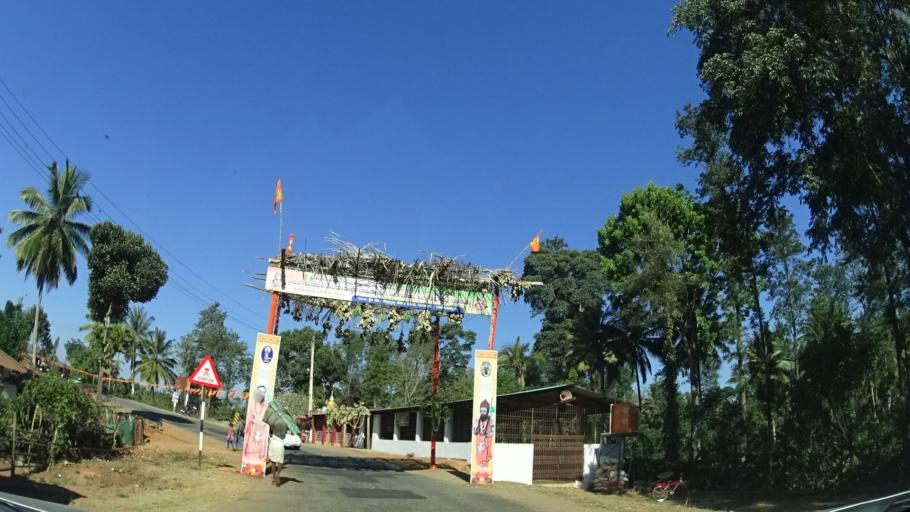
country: IN
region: Karnataka
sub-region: Chikmagalur
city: Koppa
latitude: 13.3531
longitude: 75.4713
